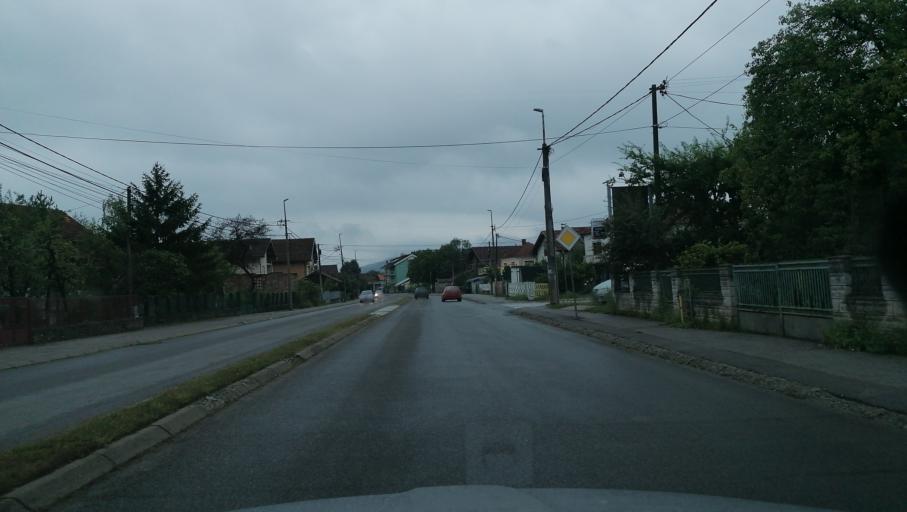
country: RS
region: Central Serbia
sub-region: Rasinski Okrug
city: Krusevac
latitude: 43.5838
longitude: 21.3056
